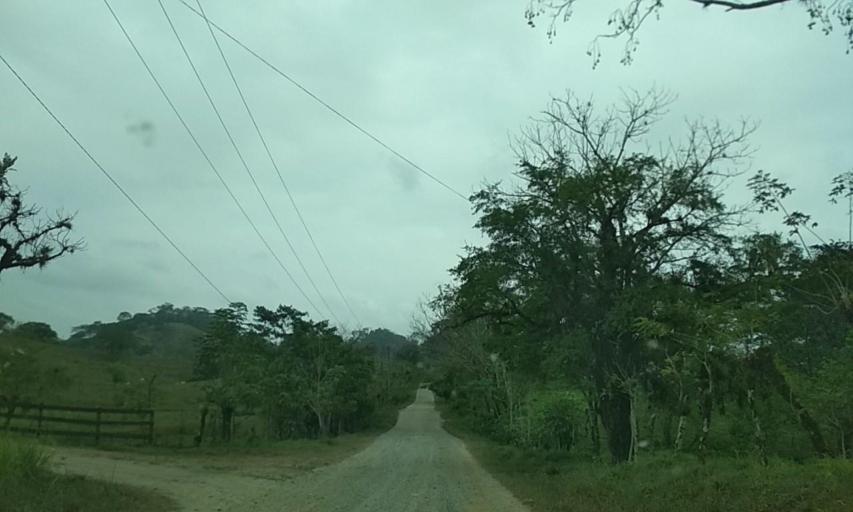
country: MX
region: Veracruz
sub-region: Uxpanapa
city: Poblado 10
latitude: 17.4811
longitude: -94.1237
